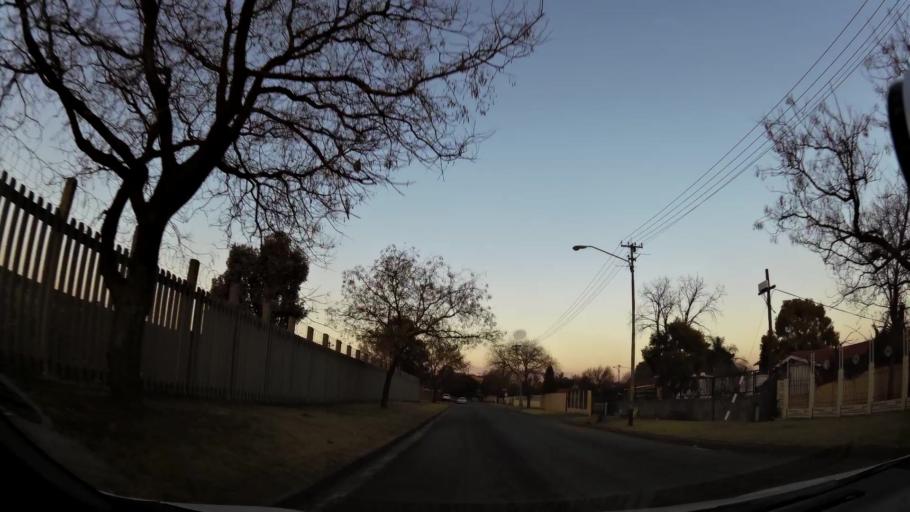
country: ZA
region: Gauteng
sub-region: Ekurhuleni Metropolitan Municipality
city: Germiston
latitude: -26.2692
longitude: 28.1612
